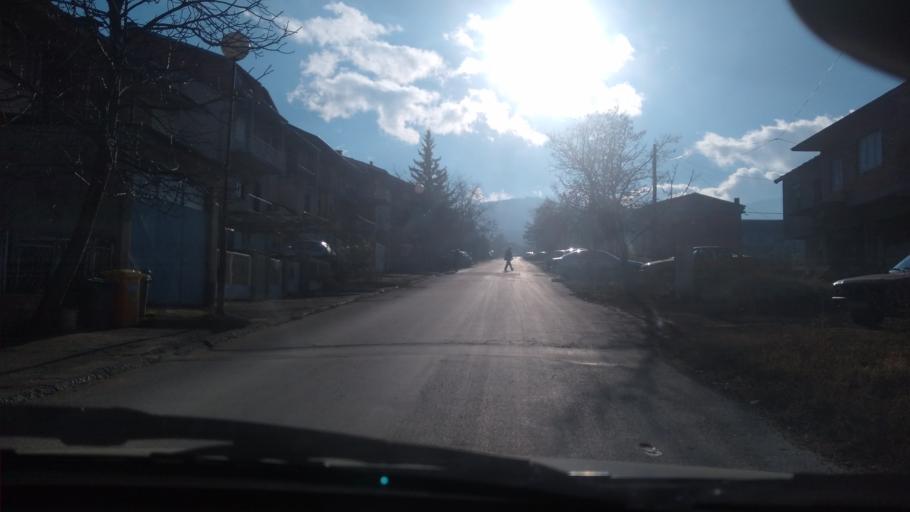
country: MK
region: Bitola
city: Bitola
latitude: 41.0061
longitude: 21.3447
